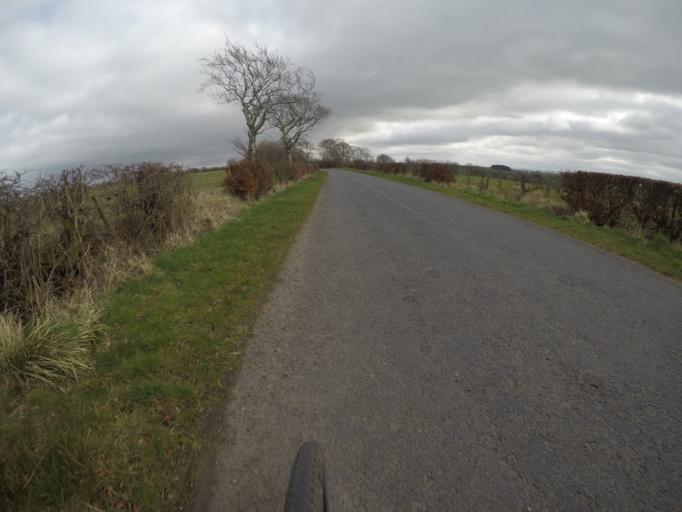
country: GB
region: Scotland
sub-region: North Ayrshire
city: Springside
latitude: 55.6689
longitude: -4.5815
